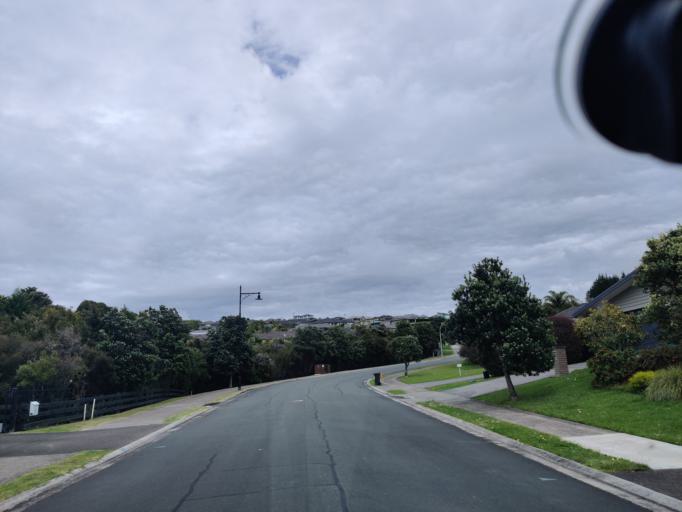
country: NZ
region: Auckland
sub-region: Auckland
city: Rothesay Bay
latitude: -36.5669
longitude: 174.6880
